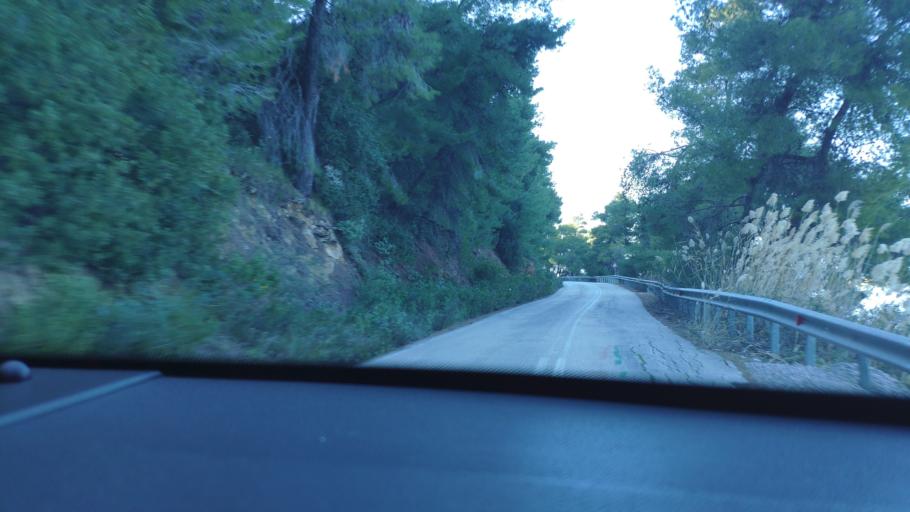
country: GR
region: Peloponnese
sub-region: Nomos Korinthias
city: Agioi Theodoroi
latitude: 38.0587
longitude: 23.1028
